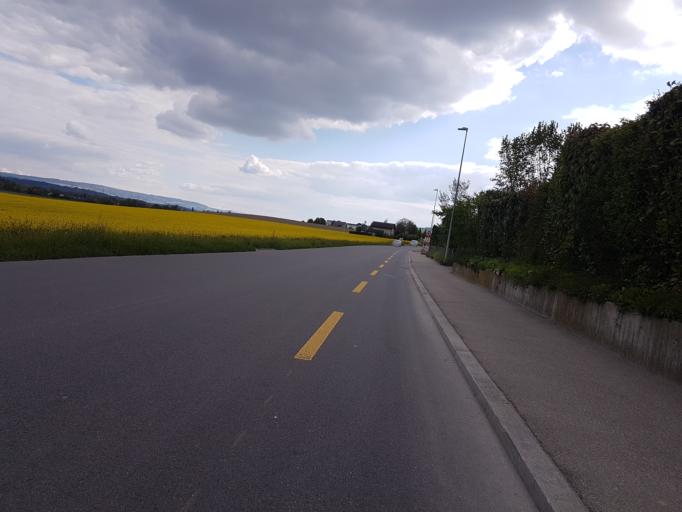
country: CH
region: Bern
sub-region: Biel/Bienne District
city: Orpund
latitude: 47.1456
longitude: 7.3181
